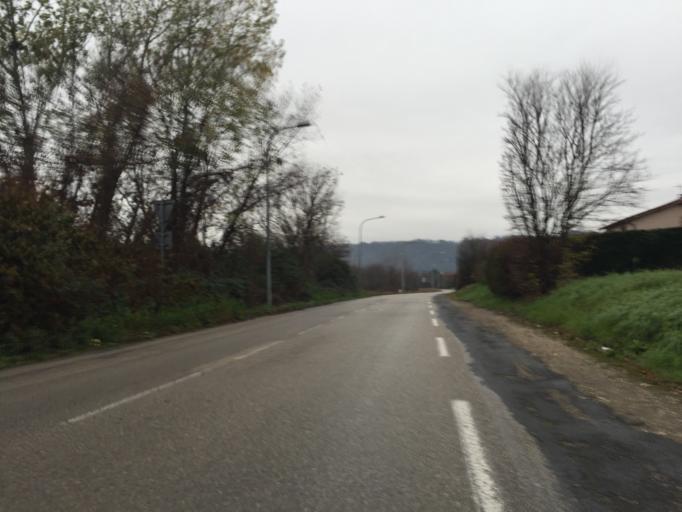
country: FR
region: Rhone-Alpes
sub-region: Departement de l'Ain
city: Saint-Maurice-de-Beynost
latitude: 45.8234
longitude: 4.9762
